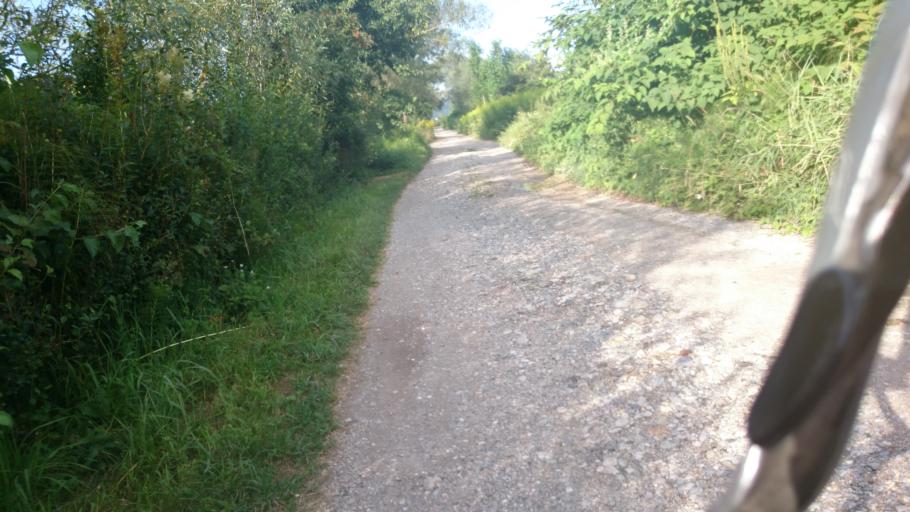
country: SI
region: Ljubljana
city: Ljubljana
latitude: 46.0182
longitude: 14.5001
